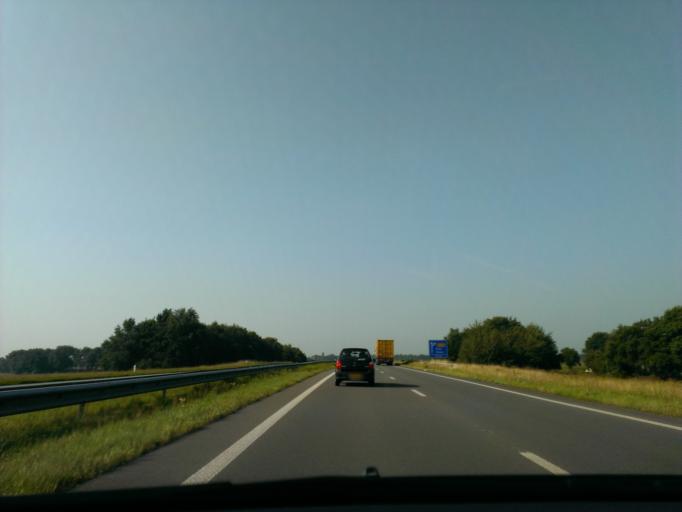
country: NL
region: Drenthe
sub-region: Gemeente Coevorden
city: Sleen
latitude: 52.7563
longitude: 6.8353
